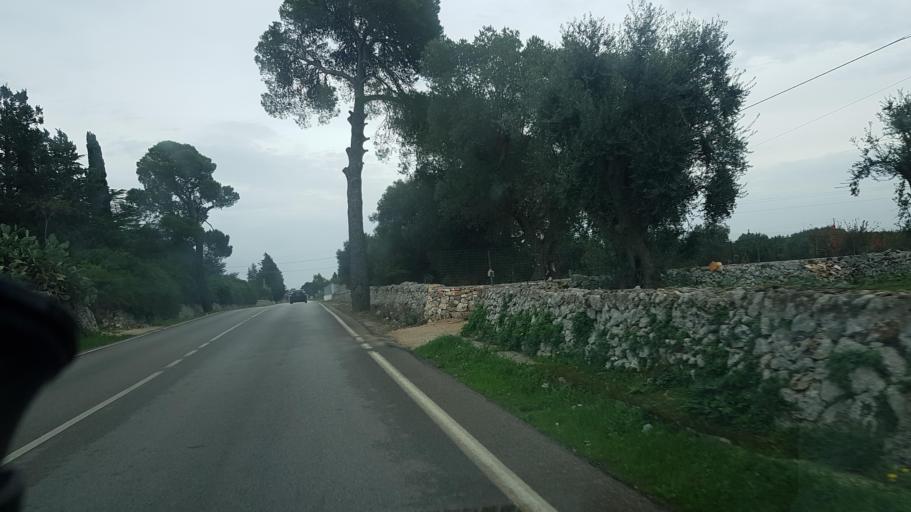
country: IT
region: Apulia
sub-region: Provincia di Brindisi
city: Carovigno
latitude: 40.7093
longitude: 17.6403
